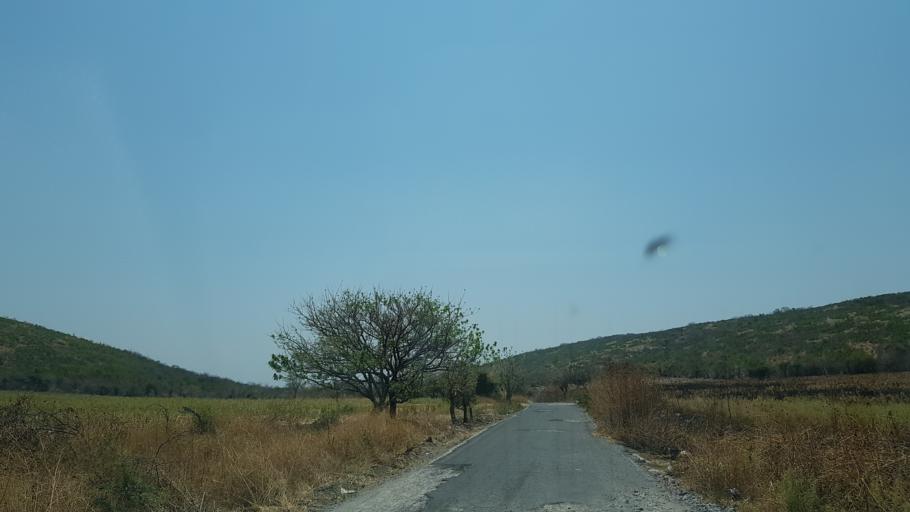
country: MX
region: Puebla
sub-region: Atzitzihuacan
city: San Miguel Aguacomulican
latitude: 18.7991
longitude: -98.5466
